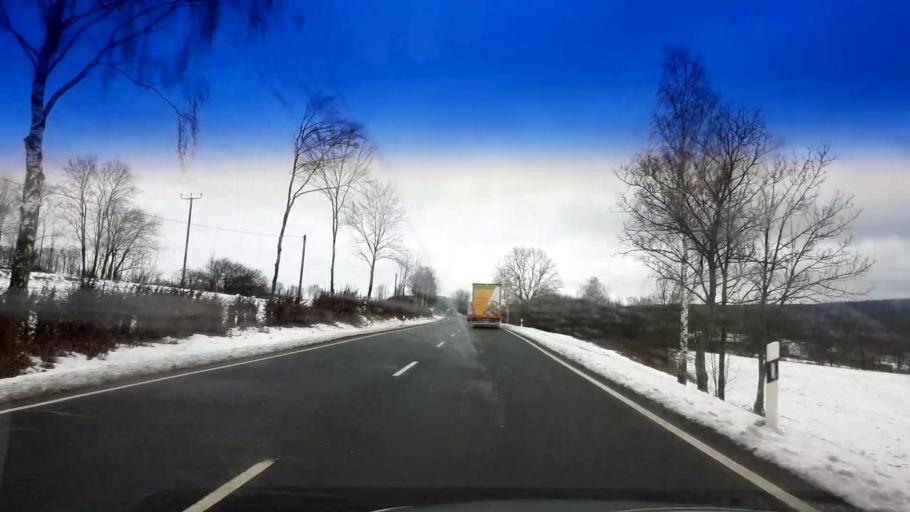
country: DE
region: Bavaria
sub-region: Upper Palatinate
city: Erbendorf
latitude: 49.8528
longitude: 11.9751
